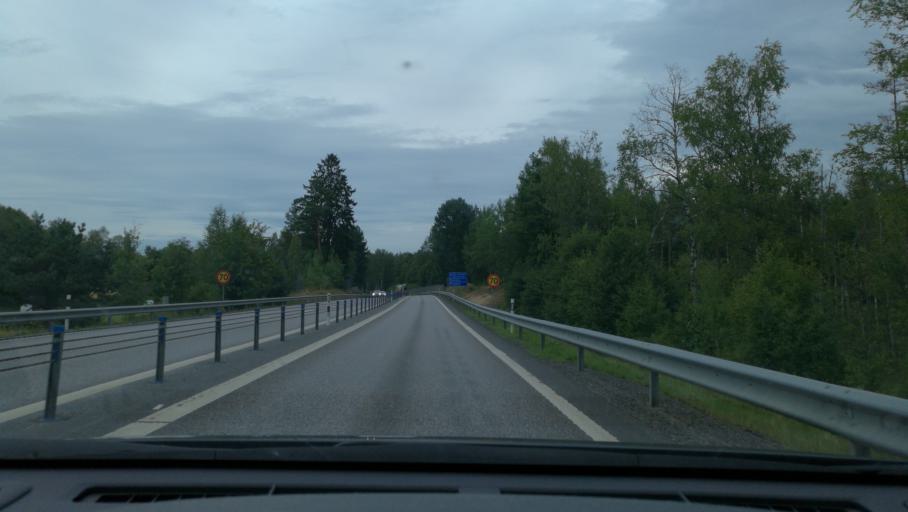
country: SE
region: Soedermanland
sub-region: Katrineholms Kommun
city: Katrineholm
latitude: 58.8507
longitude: 16.2058
